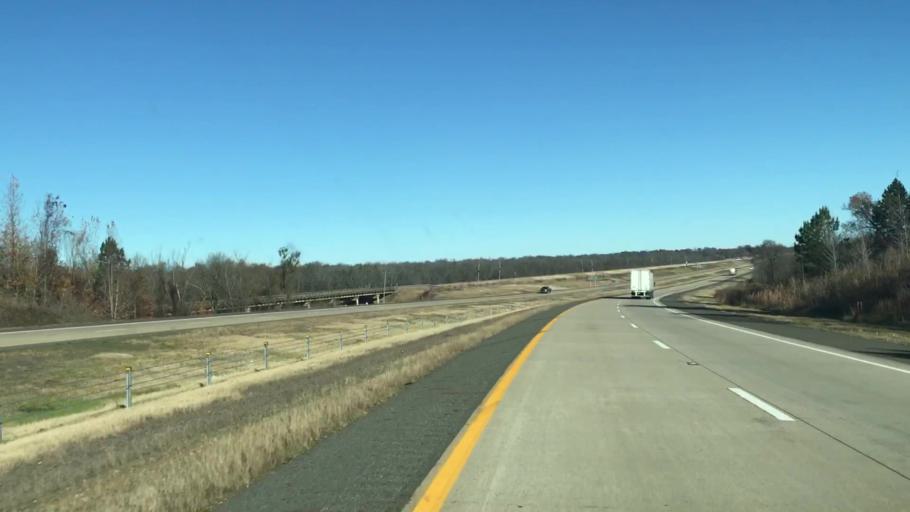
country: US
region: Texas
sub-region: Cass County
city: Queen City
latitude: 33.1341
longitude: -93.8948
